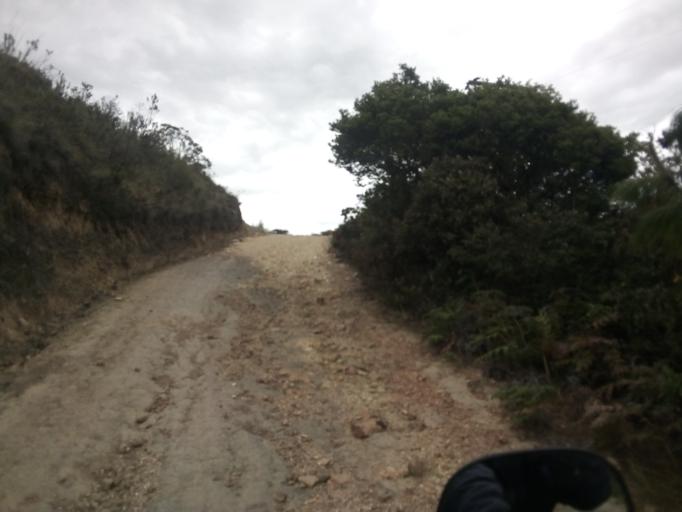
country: CO
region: Boyaca
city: Toca
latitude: 5.5962
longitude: -73.1216
